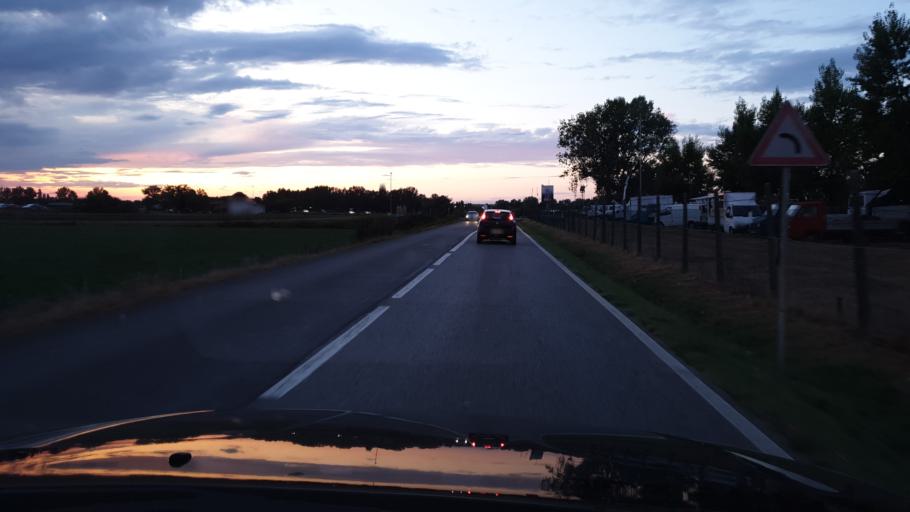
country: IT
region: Emilia-Romagna
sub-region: Provincia di Ravenna
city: Glorie
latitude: 44.4916
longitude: 12.0657
